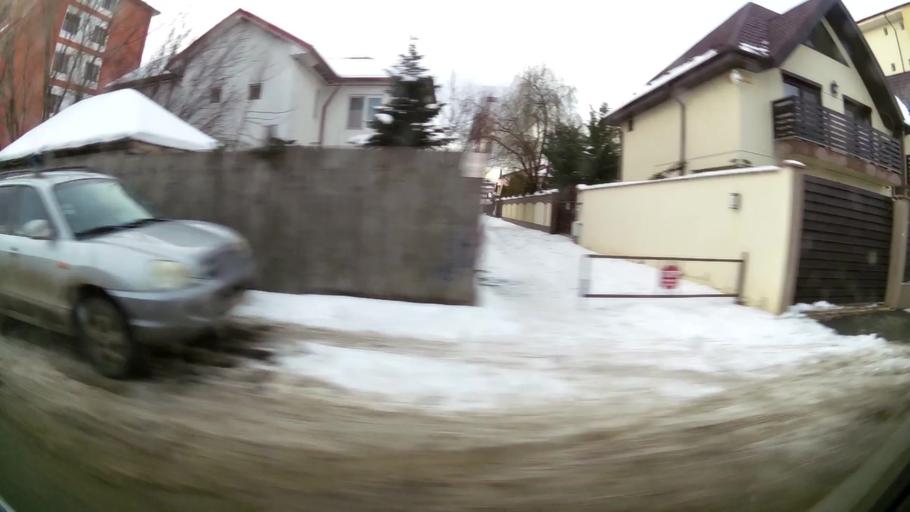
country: RO
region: Ilfov
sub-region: Comuna Popesti-Leordeni
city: Popesti-Leordeni
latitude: 44.3641
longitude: 26.1523
